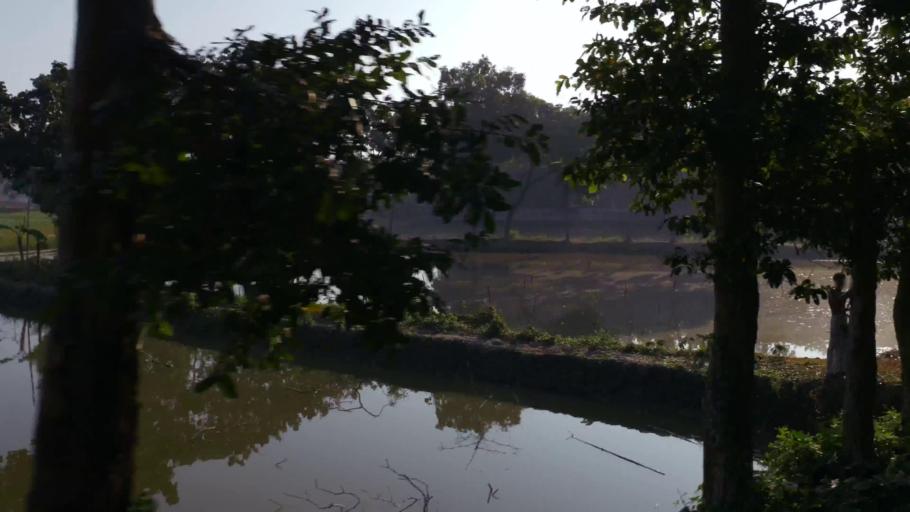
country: BD
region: Dhaka
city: Jamalpur
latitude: 24.9055
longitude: 89.9704
